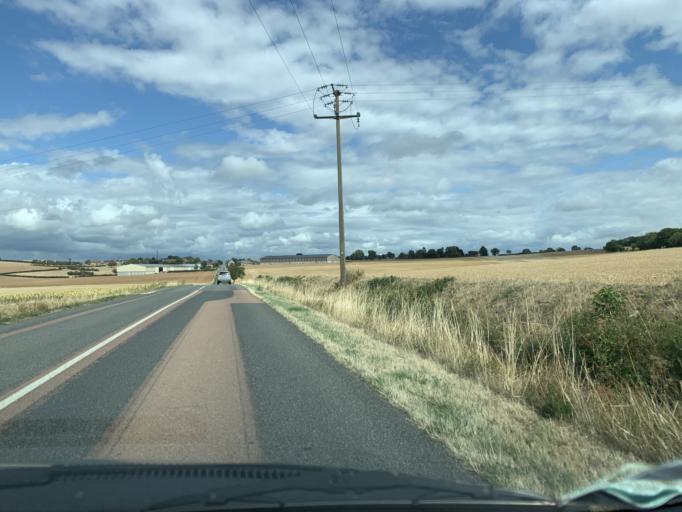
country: FR
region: Bourgogne
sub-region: Departement de la Nievre
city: Varzy
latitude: 47.3699
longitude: 3.4189
